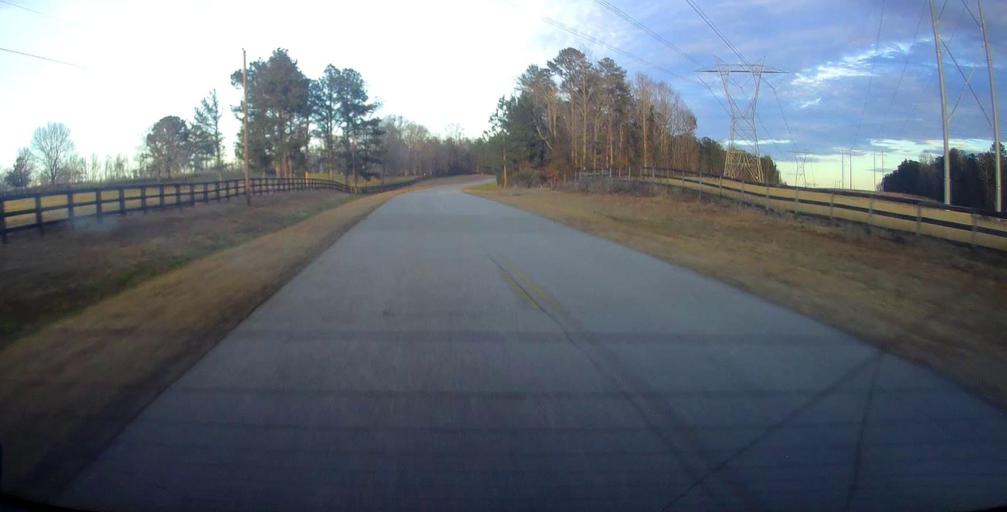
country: US
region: Georgia
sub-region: Harris County
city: Hamilton
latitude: 32.6040
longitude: -84.8764
